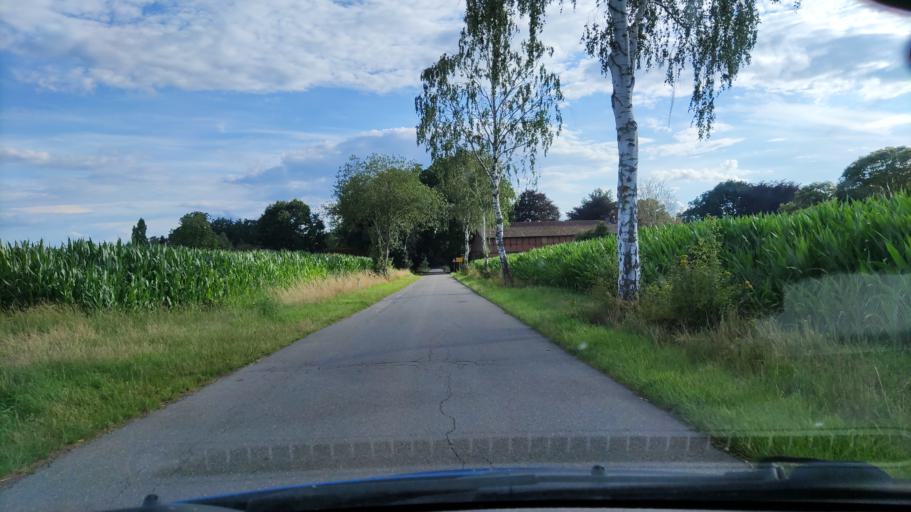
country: DE
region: Lower Saxony
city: Boitze
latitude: 53.1521
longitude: 10.7504
